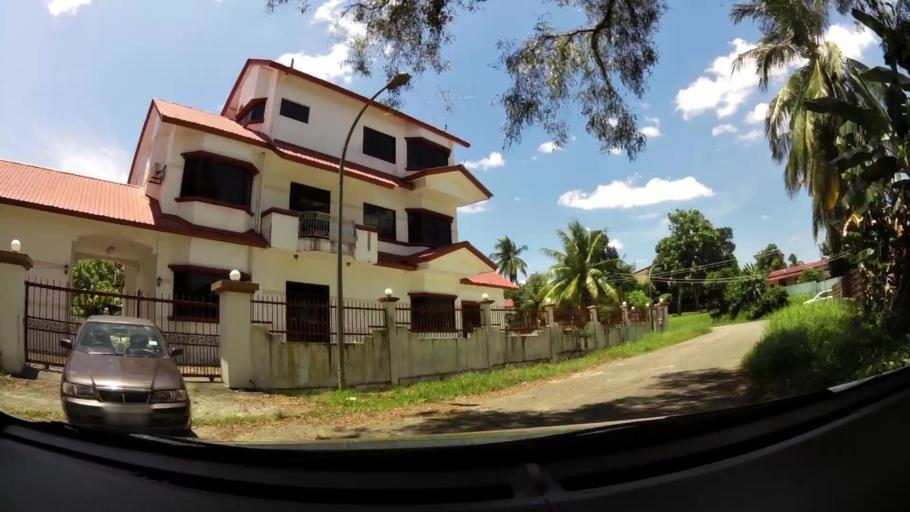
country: BN
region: Brunei and Muara
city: Bandar Seri Begawan
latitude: 4.9442
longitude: 114.9589
